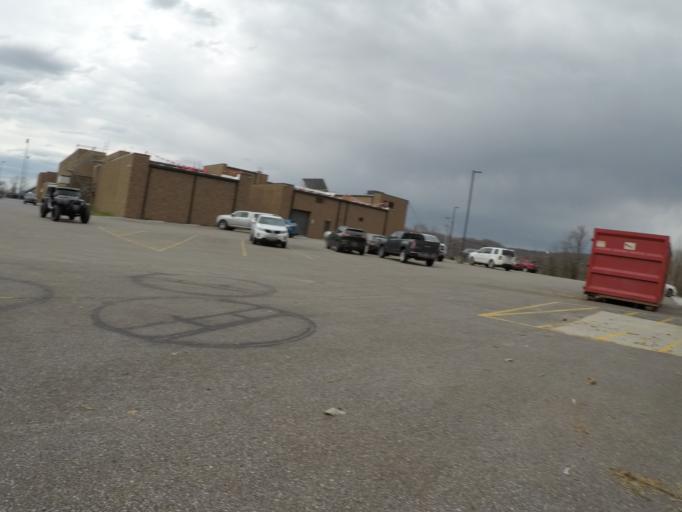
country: US
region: West Virginia
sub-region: Cabell County
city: Huntington
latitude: 38.4229
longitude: -82.4873
